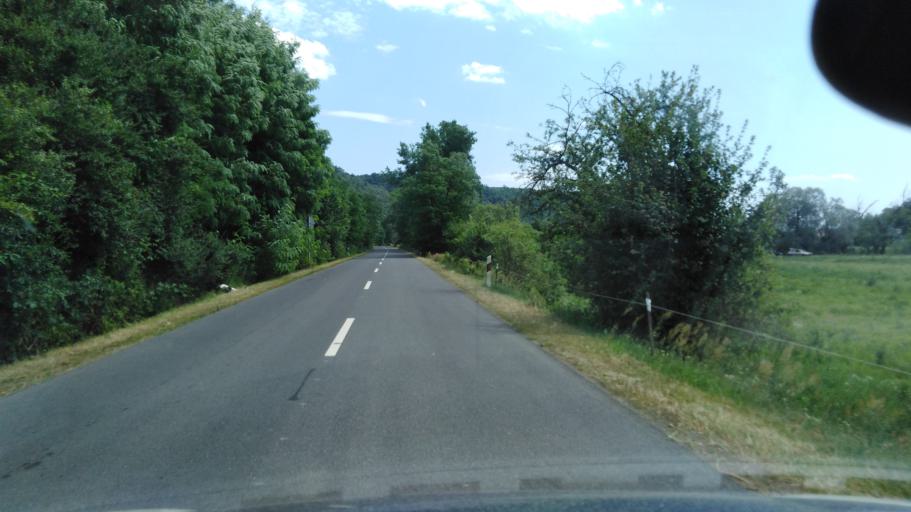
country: HU
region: Nograd
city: Szecseny
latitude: 48.1997
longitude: 19.5275
